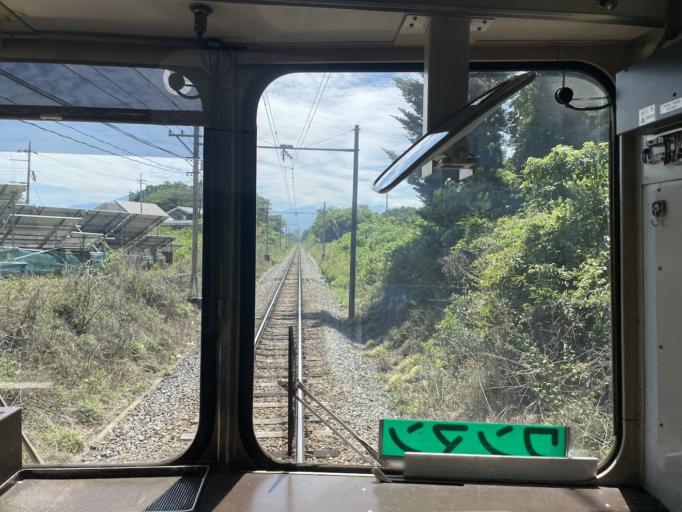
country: JP
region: Saitama
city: Chichibu
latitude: 36.0423
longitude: 139.1005
